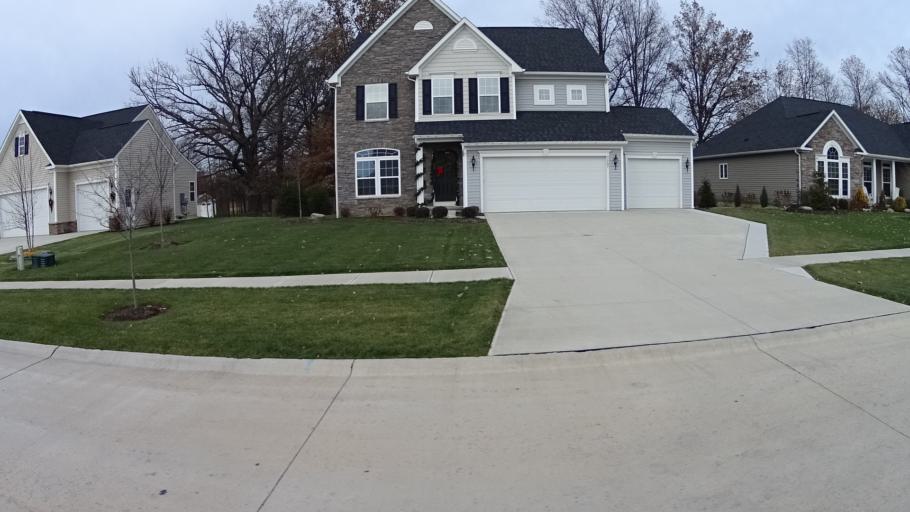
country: US
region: Ohio
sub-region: Lorain County
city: North Ridgeville
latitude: 41.3877
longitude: -82.0548
